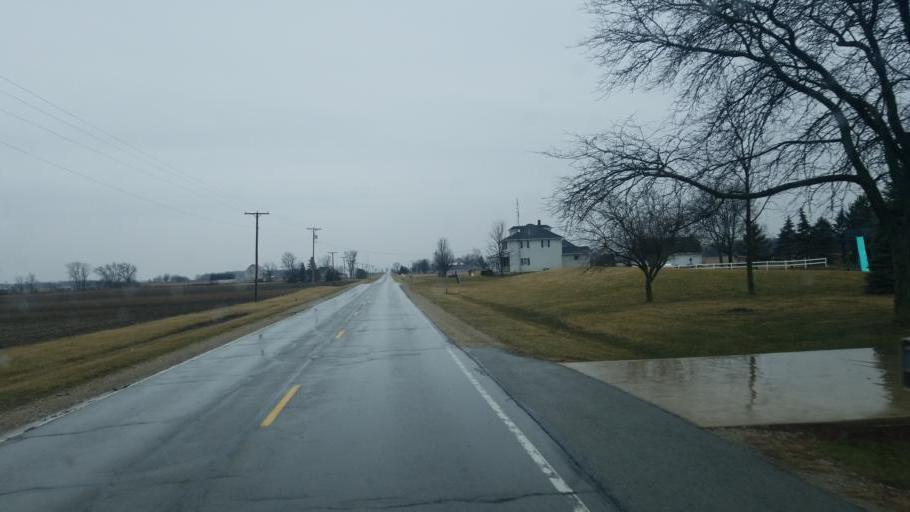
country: US
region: Indiana
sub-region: Adams County
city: Geneva
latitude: 40.6185
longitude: -85.0411
